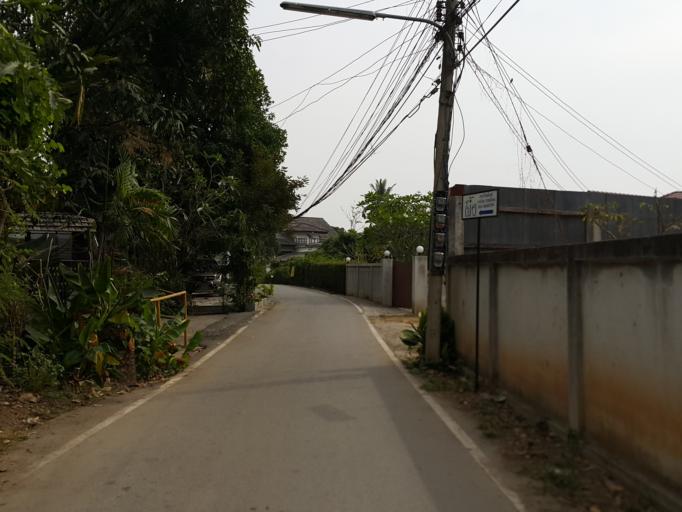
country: TH
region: Chiang Mai
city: Saraphi
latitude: 18.6773
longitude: 99.0418
